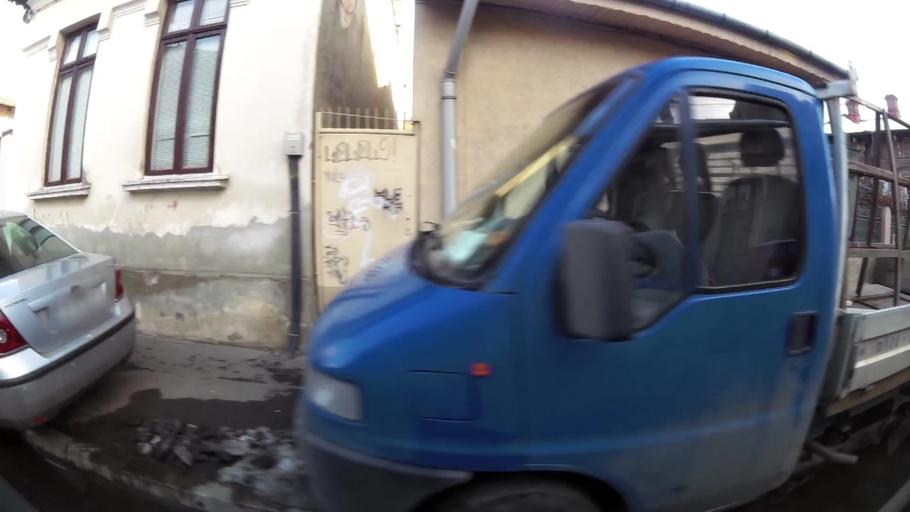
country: RO
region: Bucuresti
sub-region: Municipiul Bucuresti
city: Bucharest
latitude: 44.4373
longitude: 26.1239
